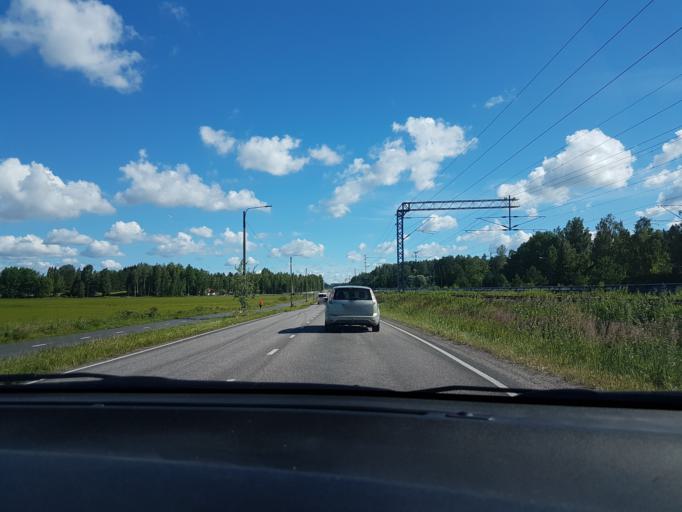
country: FI
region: Uusimaa
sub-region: Helsinki
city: Kerava
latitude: 60.3612
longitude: 25.0841
